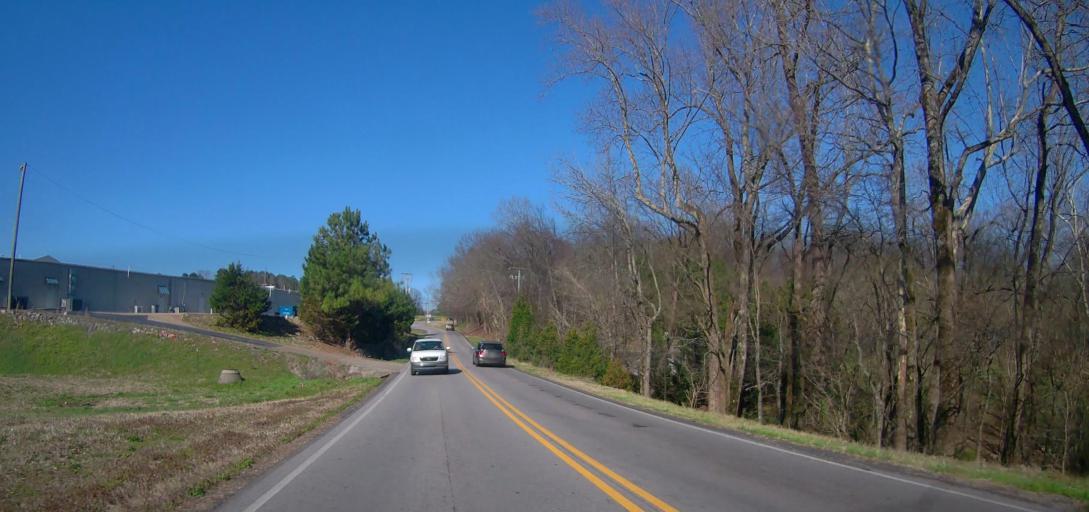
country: US
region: Alabama
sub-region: Lauderdale County
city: East Florence
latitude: 34.8336
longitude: -87.6108
